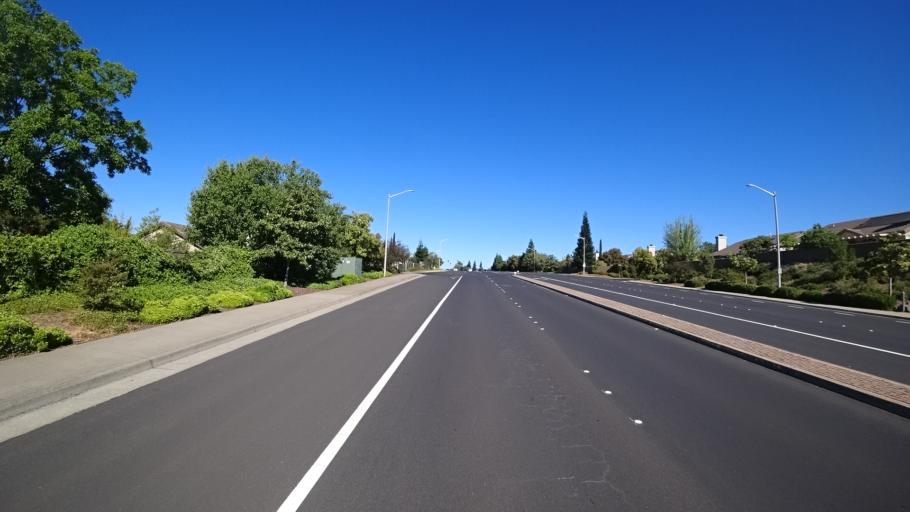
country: US
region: California
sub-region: Placer County
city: Rocklin
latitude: 38.8170
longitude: -121.2710
